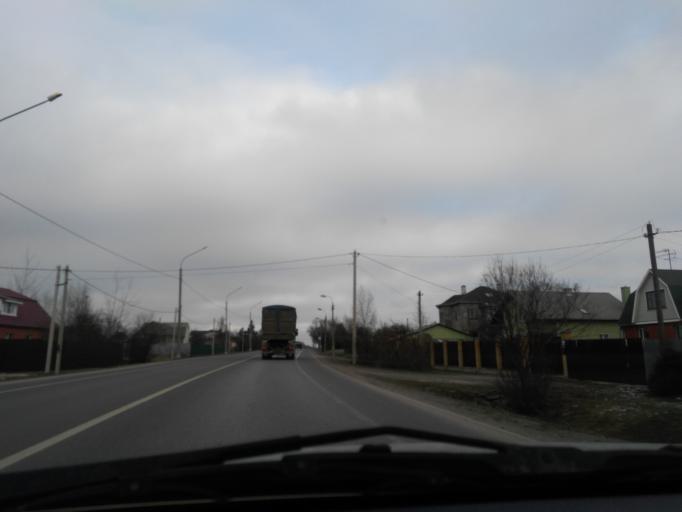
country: RU
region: Moskovskaya
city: Troitsk
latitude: 55.3713
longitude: 37.2026
